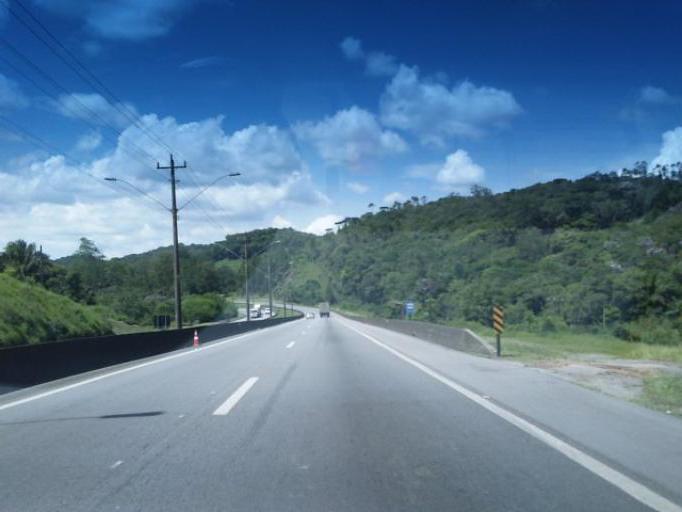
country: BR
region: Sao Paulo
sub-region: Sao Lourenco Da Serra
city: Sao Lourenco da Serra
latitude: -23.9014
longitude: -46.9900
